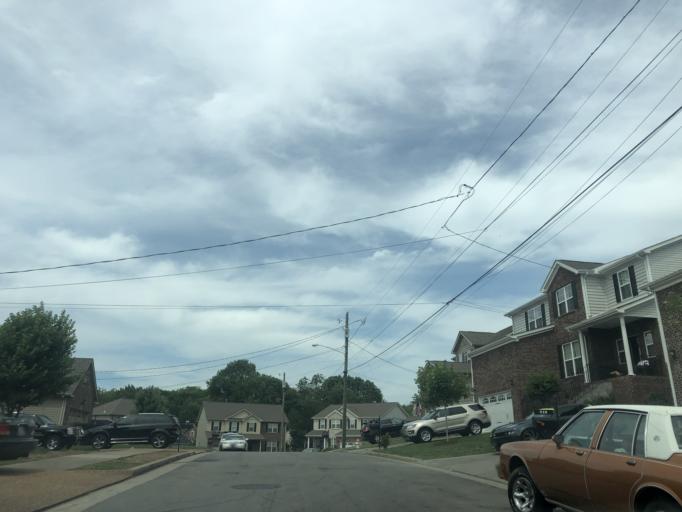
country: US
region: Tennessee
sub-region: Davidson County
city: Nashville
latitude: 36.2118
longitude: -86.8114
